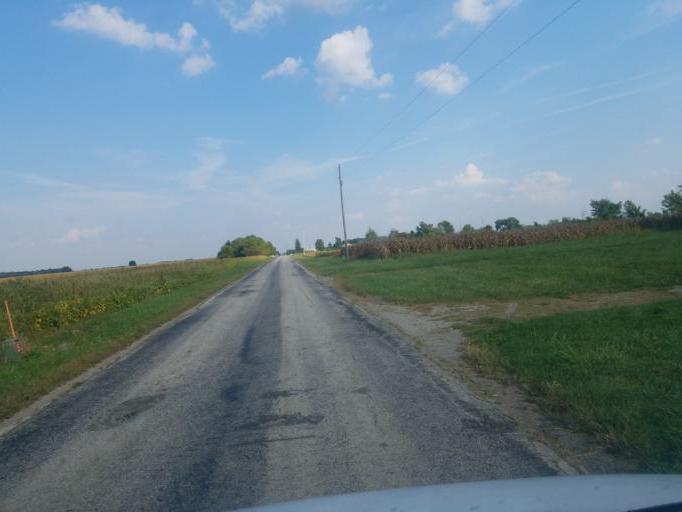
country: US
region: Ohio
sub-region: Hardin County
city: Forest
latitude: 40.9053
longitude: -83.5245
